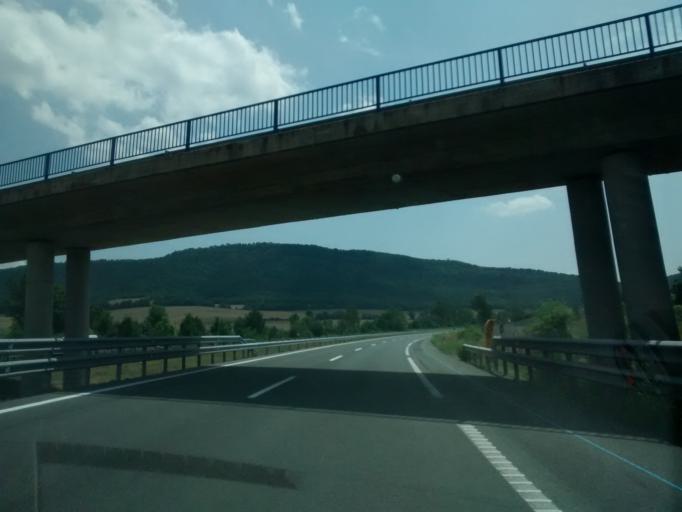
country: ES
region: Basque Country
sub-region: Provincia de Alava
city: Arminon
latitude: 42.7897
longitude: -2.8995
